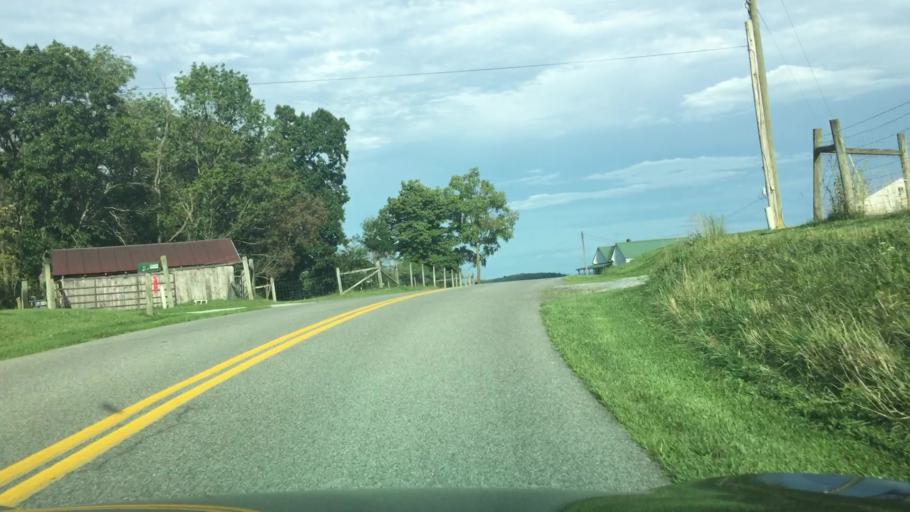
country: US
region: Virginia
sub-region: Wythe County
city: Wytheville
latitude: 36.9398
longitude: -80.9669
